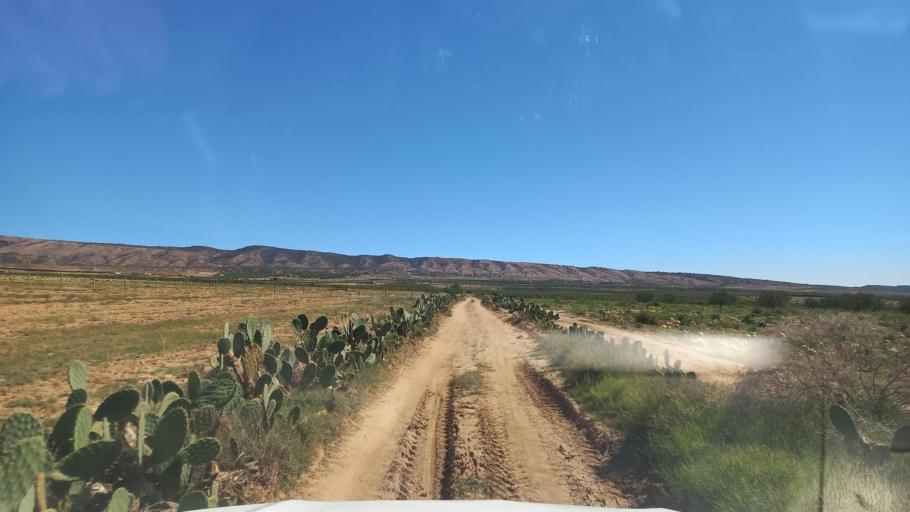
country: TN
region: Al Qasrayn
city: Sbiba
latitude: 35.3490
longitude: 9.1022
